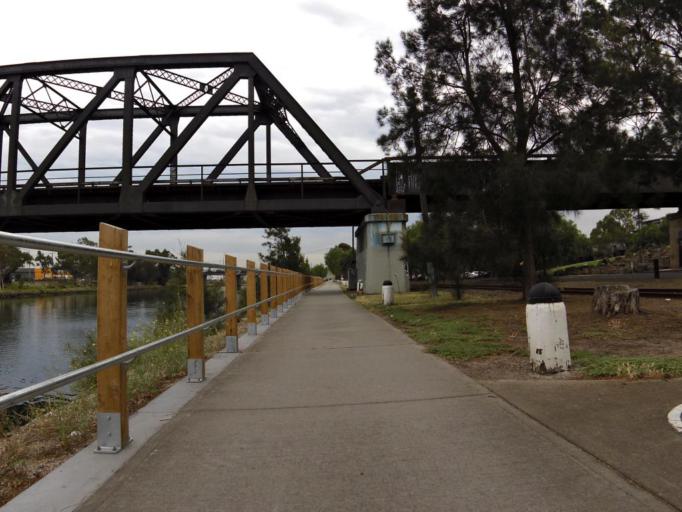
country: AU
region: Victoria
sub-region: Maribyrnong
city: Footscray
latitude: -37.8038
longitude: 144.9082
